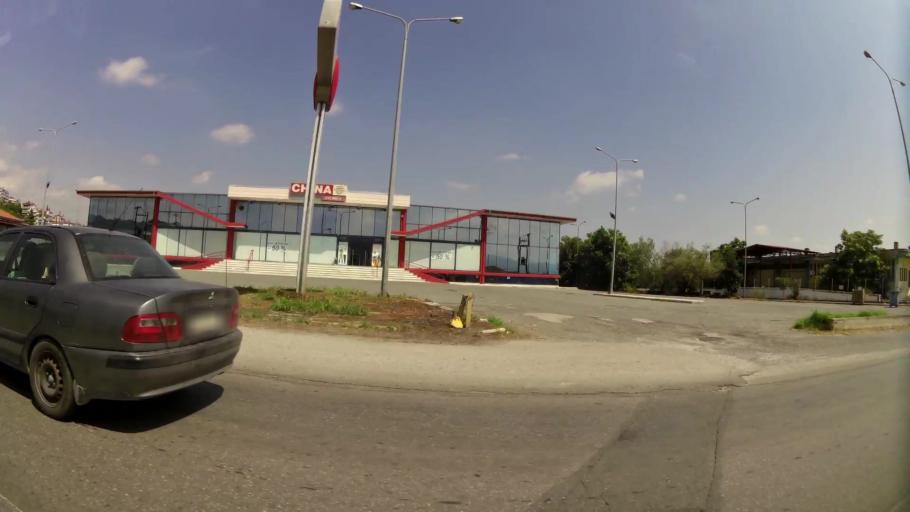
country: GR
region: Central Macedonia
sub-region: Nomos Imathias
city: Veroia
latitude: 40.5280
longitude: 22.2115
